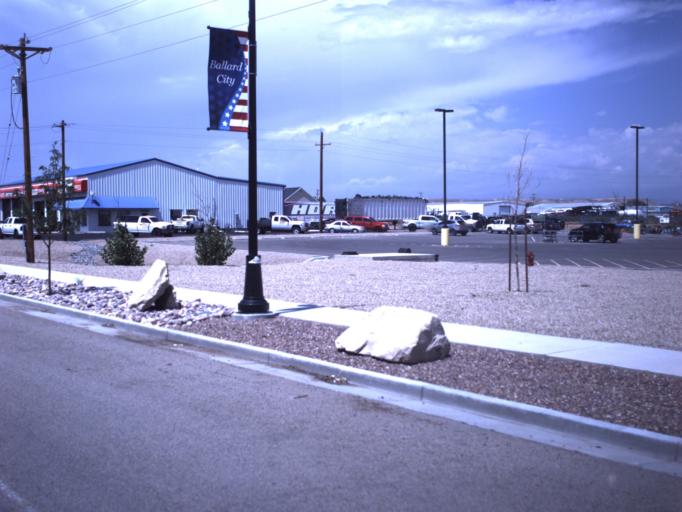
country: US
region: Utah
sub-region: Duchesne County
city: Roosevelt
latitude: 40.3023
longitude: -109.9701
